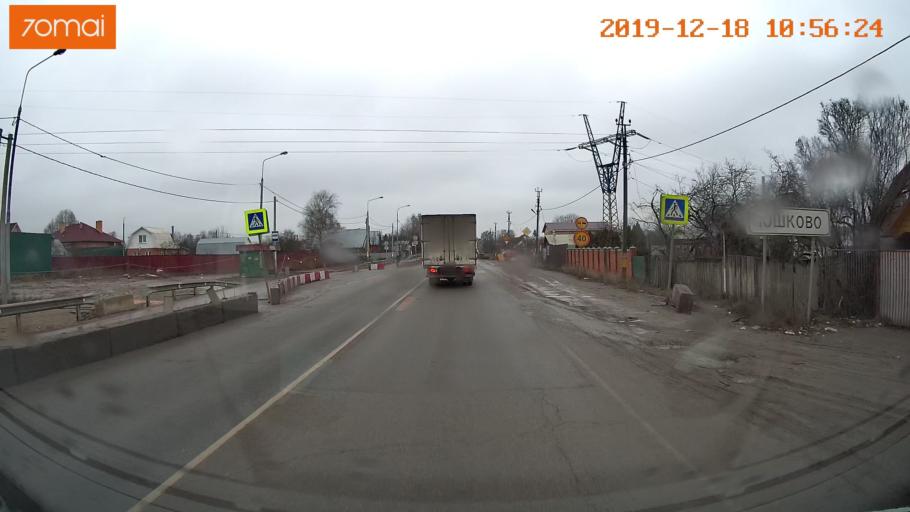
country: RU
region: Moskovskaya
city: Selyatino
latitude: 55.5408
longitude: 36.9894
